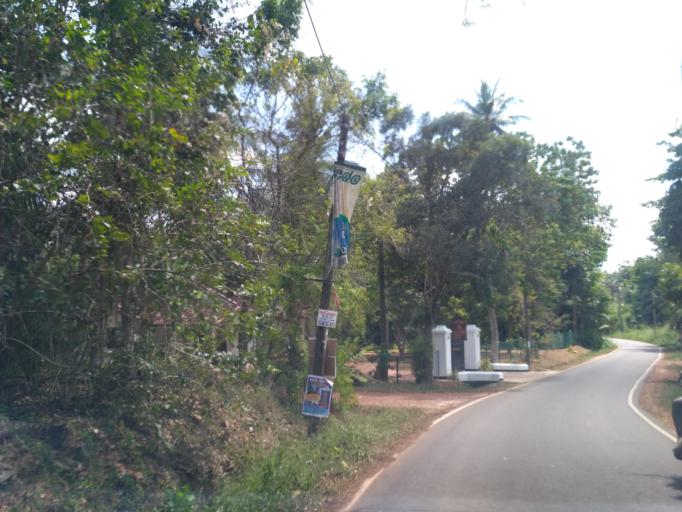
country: LK
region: North Western
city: Kuliyapitiya
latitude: 7.3333
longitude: 80.0629
